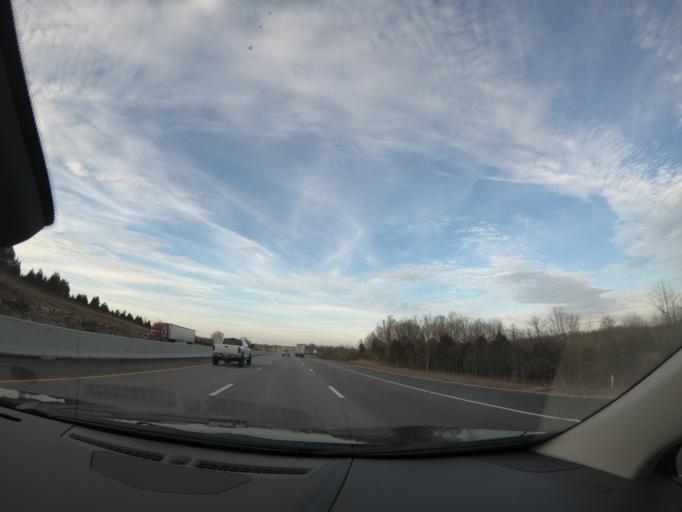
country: US
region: Kentucky
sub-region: Larue County
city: Hodgenville
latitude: 37.4716
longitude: -85.8817
